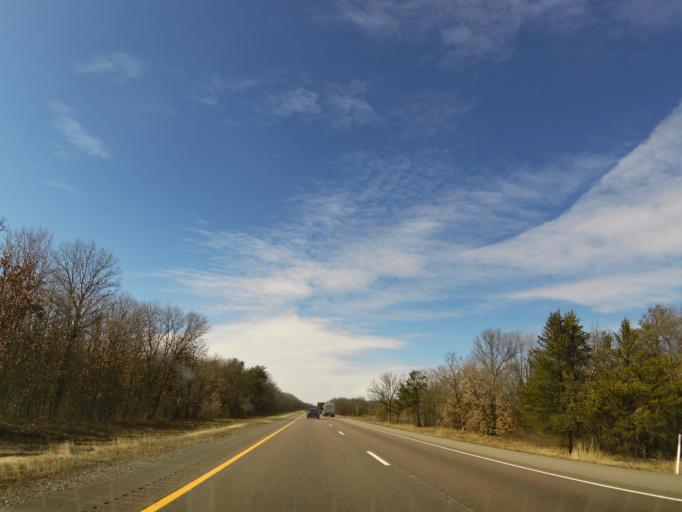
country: US
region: Wisconsin
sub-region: Jackson County
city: Black River Falls
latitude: 44.2215
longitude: -90.6929
